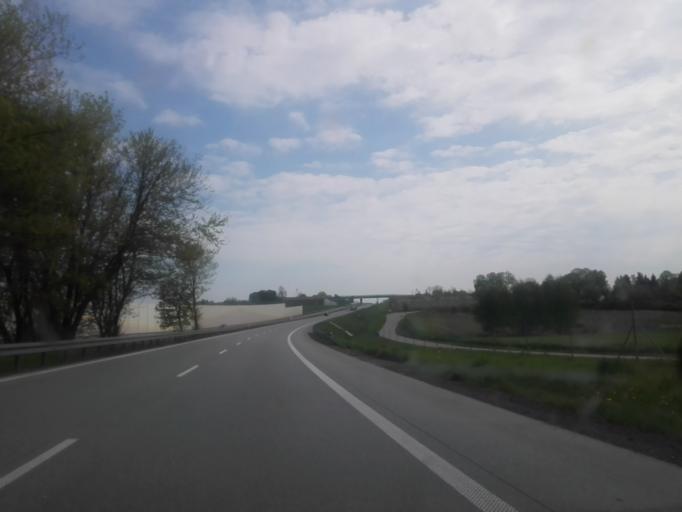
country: PL
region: Lodz Voivodeship
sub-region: Powiat skierniewicki
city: Kowiesy
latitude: 51.8772
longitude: 20.3907
